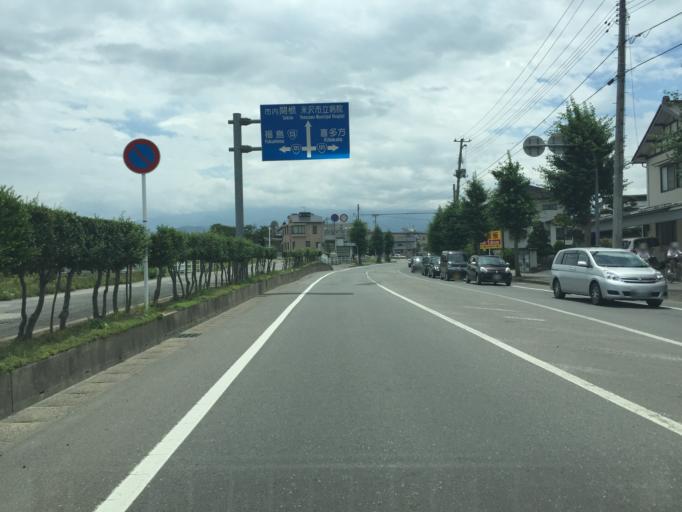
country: JP
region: Yamagata
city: Yonezawa
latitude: 37.9106
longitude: 140.1176
